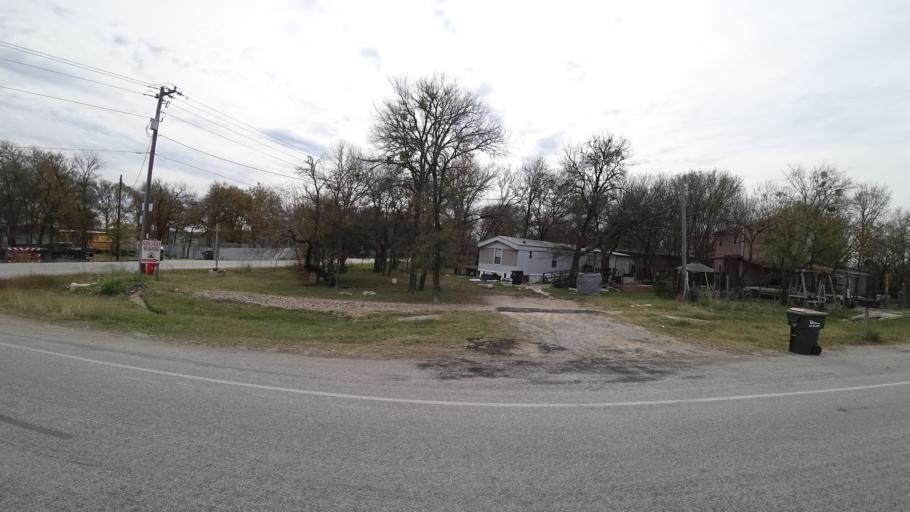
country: US
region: Texas
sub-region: Travis County
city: Garfield
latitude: 30.1387
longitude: -97.5617
